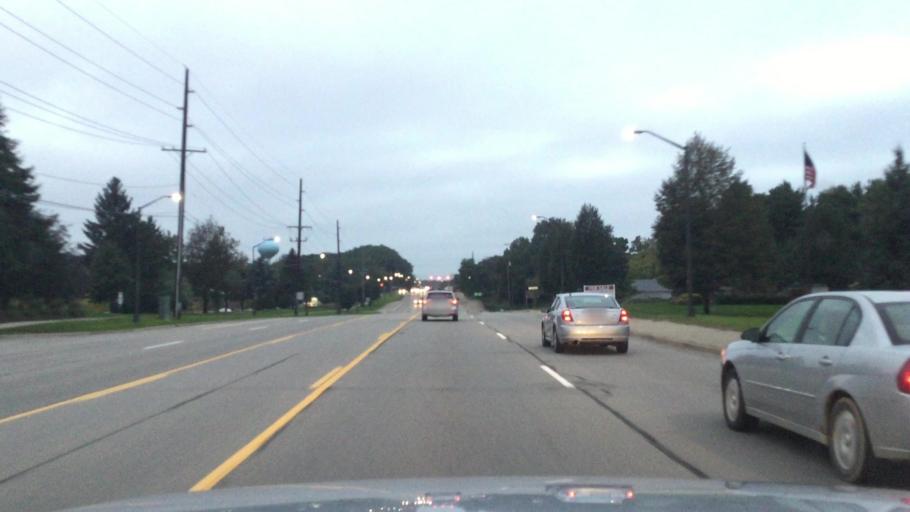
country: US
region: Michigan
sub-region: Oakland County
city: Clarkston
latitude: 42.7238
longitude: -83.4253
